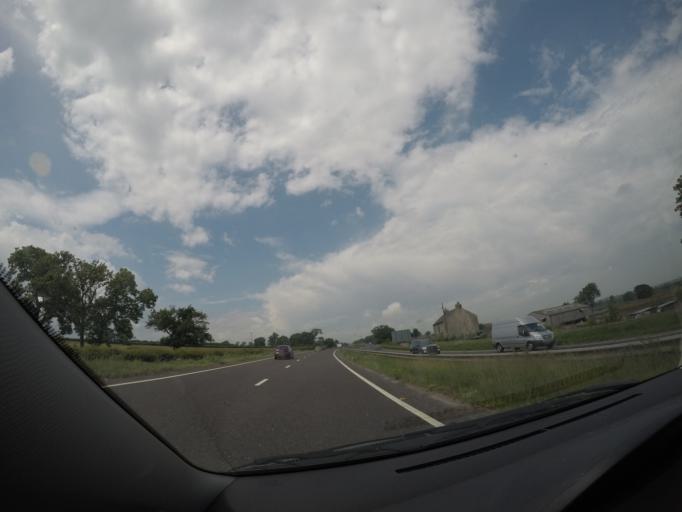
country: GB
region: England
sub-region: County Durham
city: Hutton Magna
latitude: 54.4977
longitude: -1.8326
